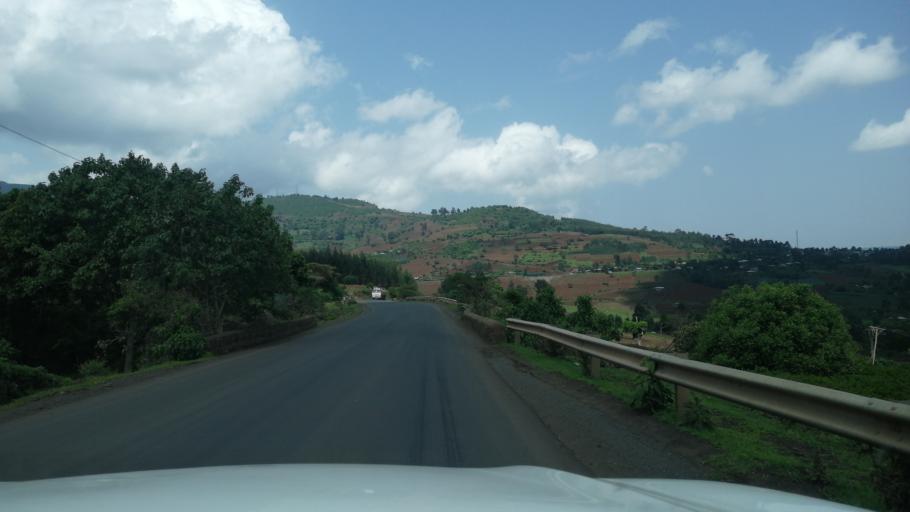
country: ET
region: Oromiya
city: Gedo
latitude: 8.9863
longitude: 37.6065
